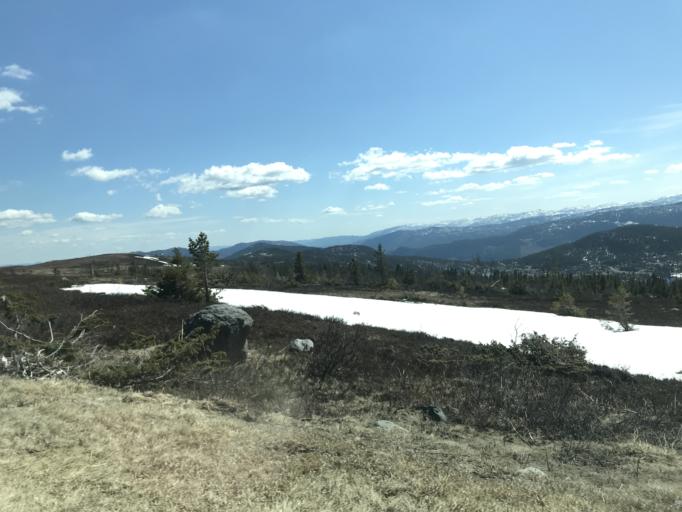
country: NO
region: Telemark
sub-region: Tinn
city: Rjukan
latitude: 59.7997
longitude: 8.7604
